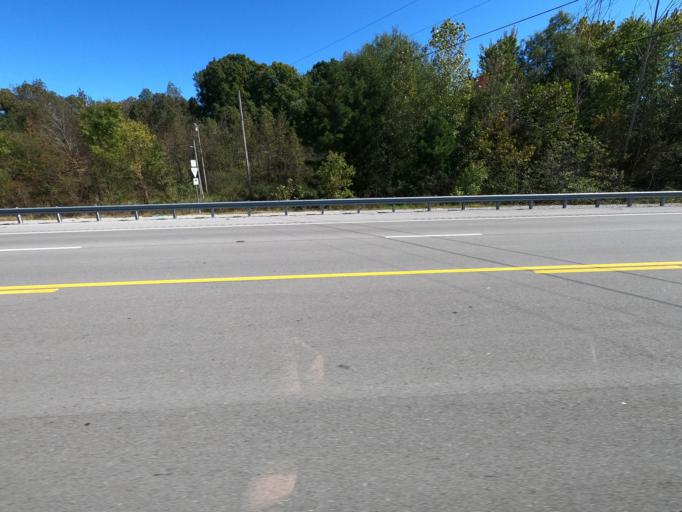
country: US
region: Tennessee
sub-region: Maury County
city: Mount Pleasant
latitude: 35.4256
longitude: -87.2819
